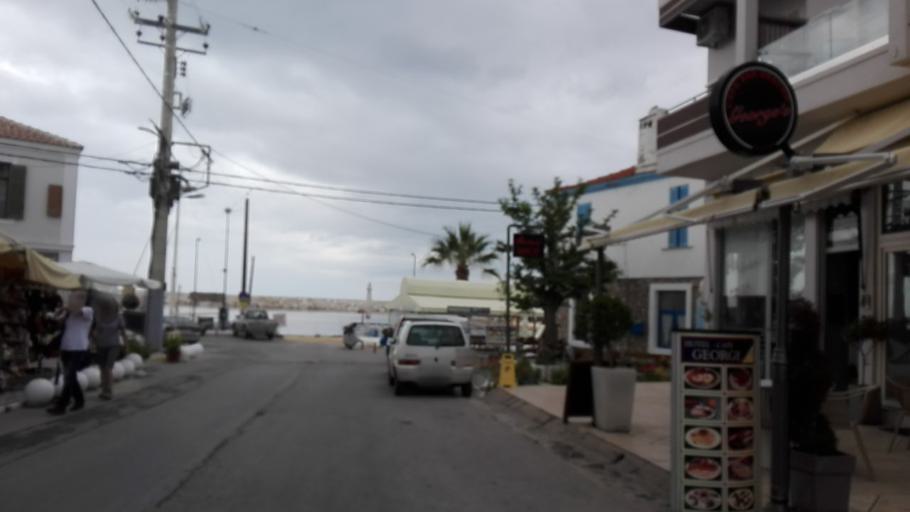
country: GR
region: East Macedonia and Thrace
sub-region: Nomos Kavalas
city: Limenaria
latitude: 40.6266
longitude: 24.5747
